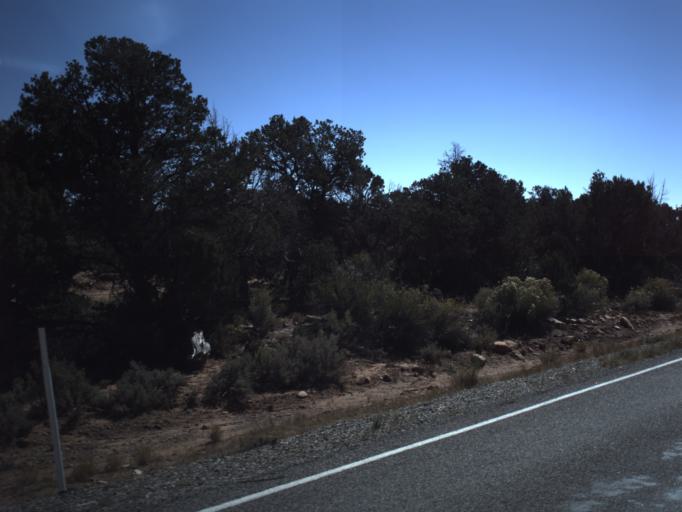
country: US
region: Utah
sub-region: San Juan County
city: Blanding
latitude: 37.5480
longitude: -109.8896
